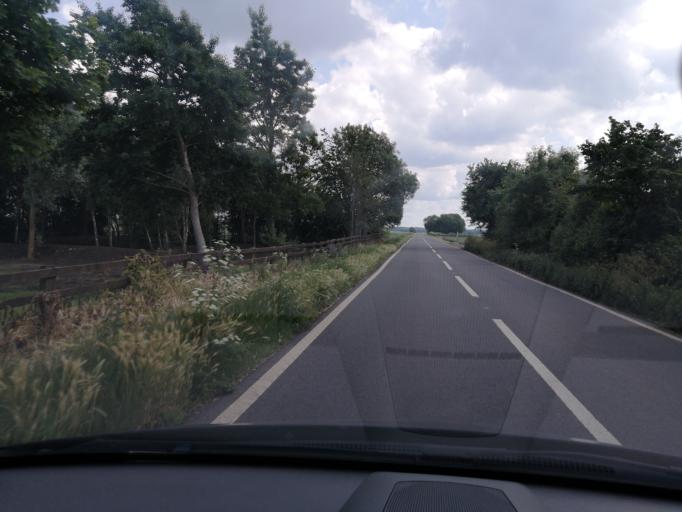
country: GB
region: England
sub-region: Cambridgeshire
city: Yaxley
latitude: 52.5078
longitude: -0.2583
